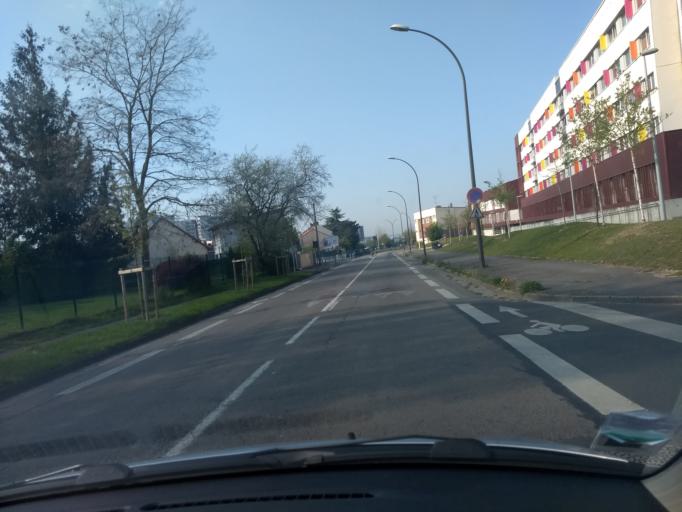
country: FR
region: Picardie
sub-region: Departement de la Somme
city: Rivery
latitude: 49.9138
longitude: 2.3185
